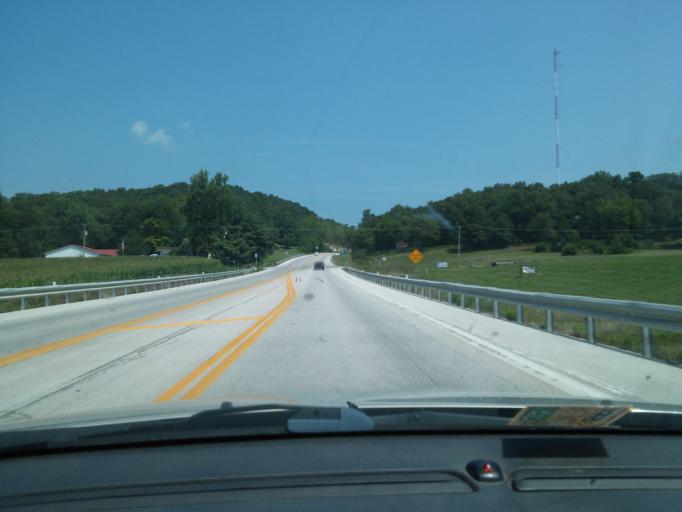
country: US
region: Missouri
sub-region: Pike County
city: Louisiana
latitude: 39.4365
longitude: -91.0797
